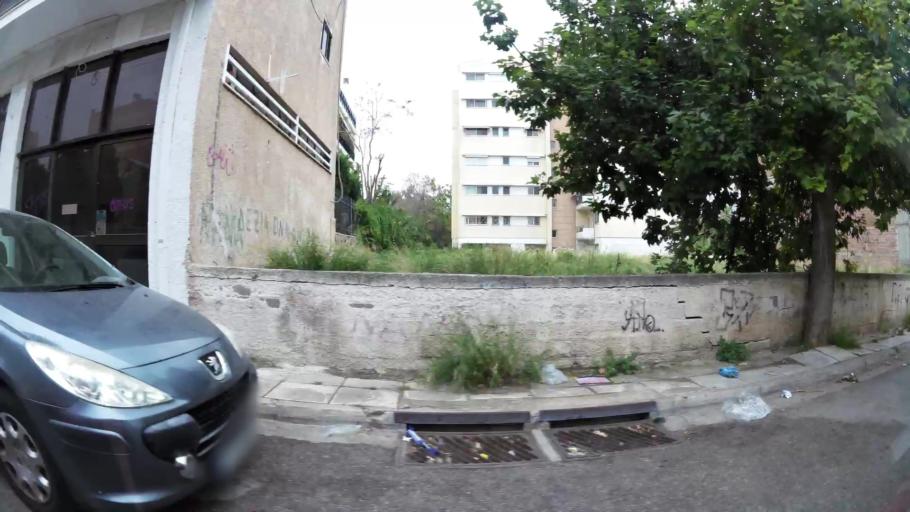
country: GR
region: Attica
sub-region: Nomarchia Athinas
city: Agioi Anargyroi
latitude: 38.0180
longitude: 23.7155
